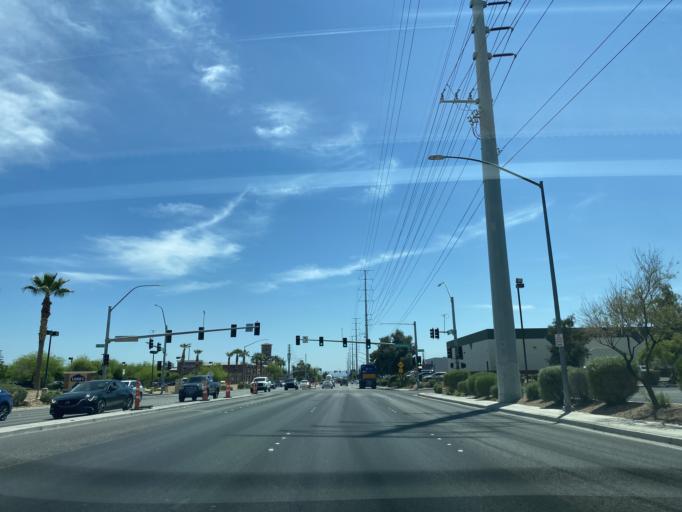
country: US
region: Nevada
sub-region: Clark County
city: North Las Vegas
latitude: 36.2425
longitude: -115.1169
